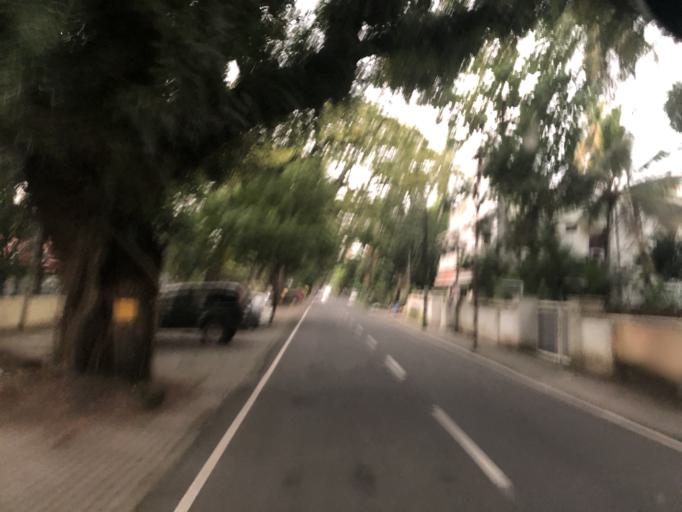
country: IN
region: Kerala
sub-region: Ernakulam
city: Cochin
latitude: 9.9574
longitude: 76.2396
